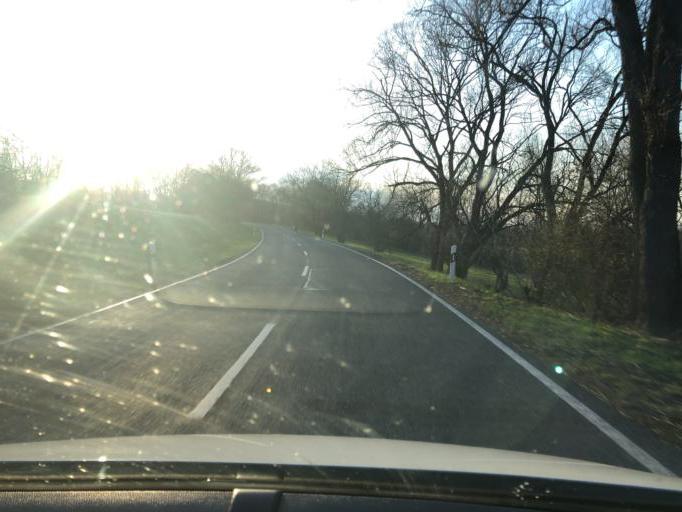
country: DE
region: Thuringia
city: Weissenborn-Luderode
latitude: 51.5416
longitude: 10.3938
